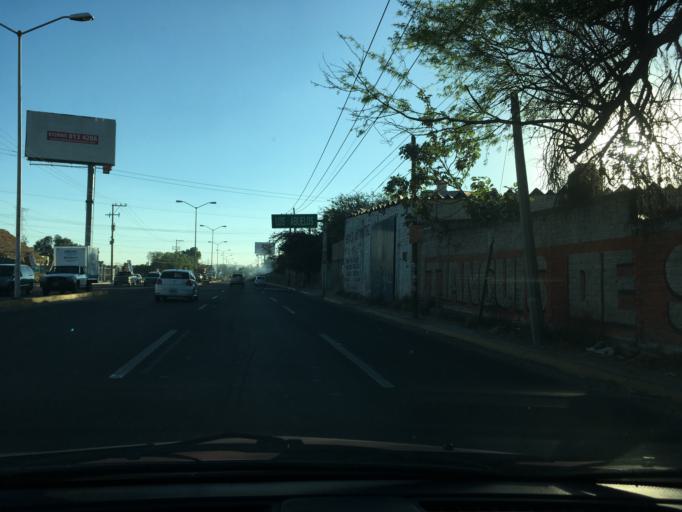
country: MX
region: Jalisco
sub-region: Tlajomulco de Zuniga
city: La Tijera
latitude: 20.5874
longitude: -103.4201
